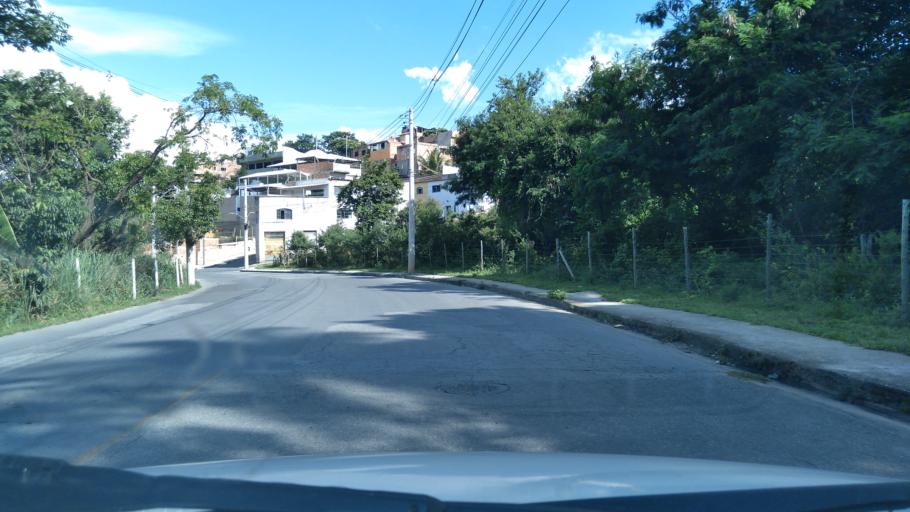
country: BR
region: Minas Gerais
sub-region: Santa Luzia
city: Santa Luzia
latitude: -19.8553
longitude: -43.8758
